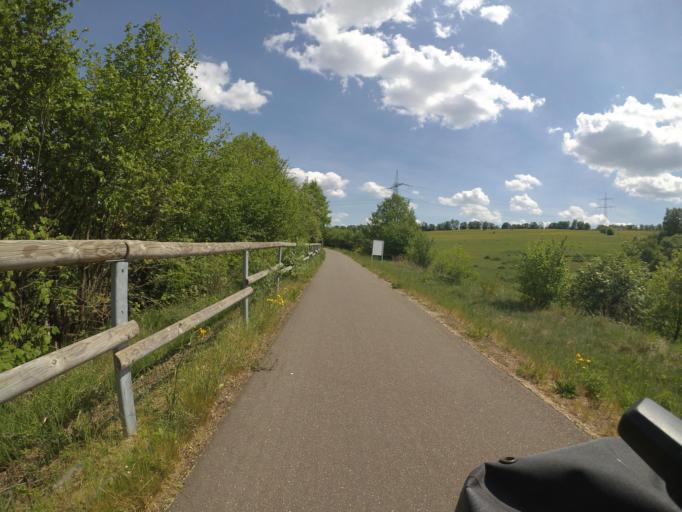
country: DE
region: Rheinland-Pfalz
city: Kerschenbach
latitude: 50.3583
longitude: 6.4899
